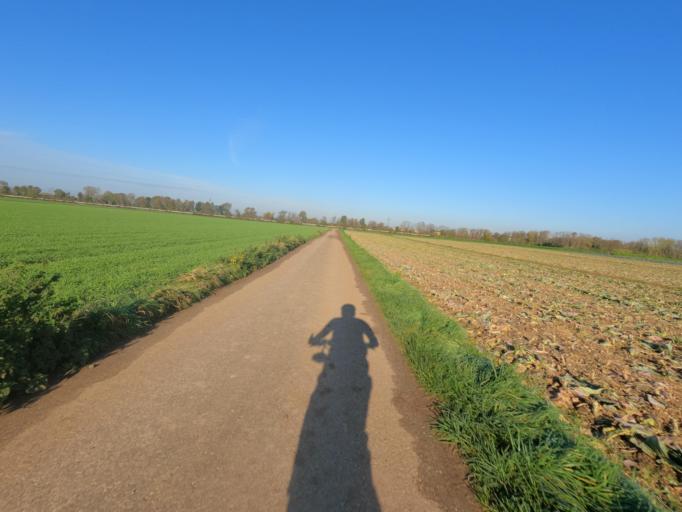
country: DE
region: North Rhine-Westphalia
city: Erkelenz
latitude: 51.0948
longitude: 6.3611
